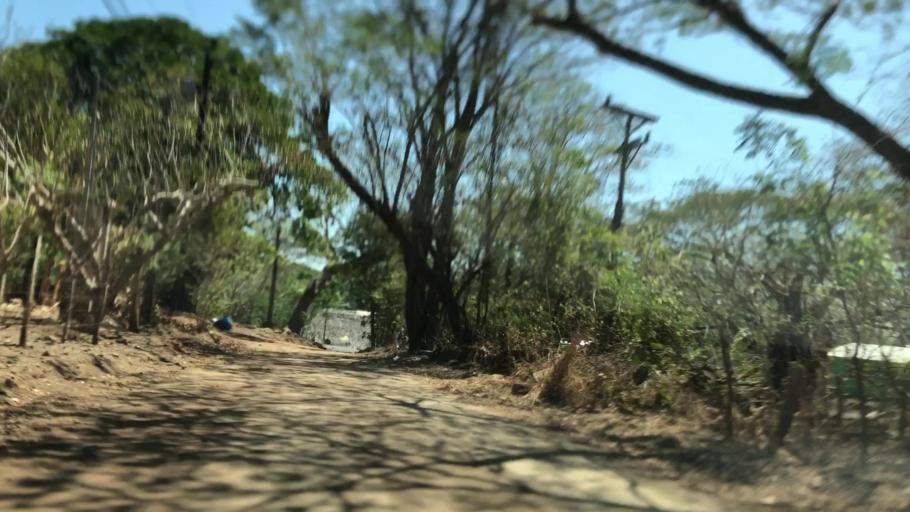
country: CR
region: Guanacaste
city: Sardinal
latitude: 10.3401
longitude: -85.8459
